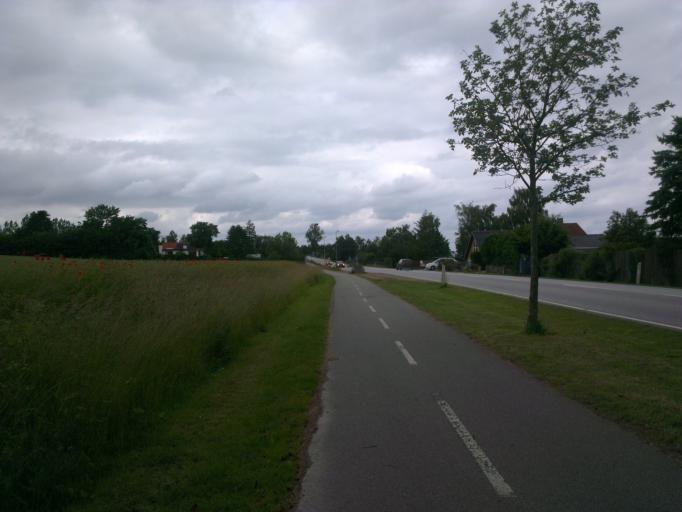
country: DK
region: Capital Region
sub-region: Frederikssund Kommune
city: Skibby
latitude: 55.6810
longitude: 11.9441
